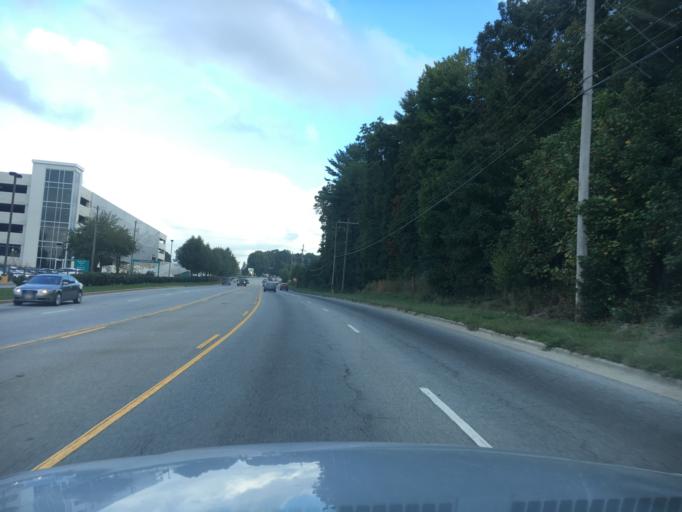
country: US
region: North Carolina
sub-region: Henderson County
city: Fletcher
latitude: 35.4333
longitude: -82.5350
